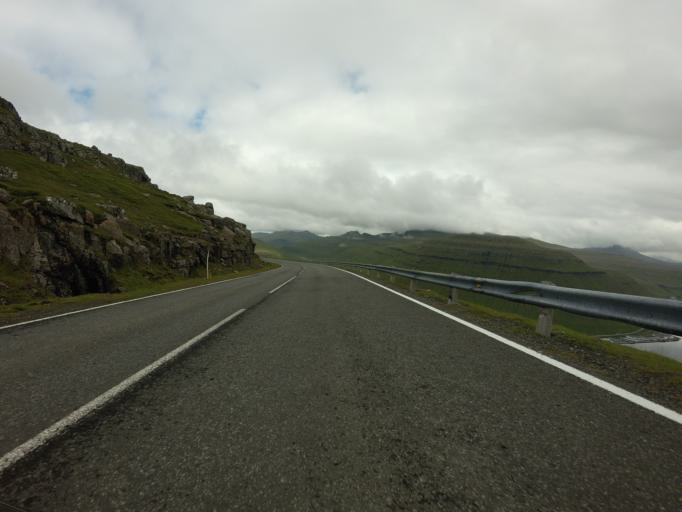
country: FO
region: Streymoy
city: Kollafjordhur
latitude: 62.0894
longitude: -6.9468
